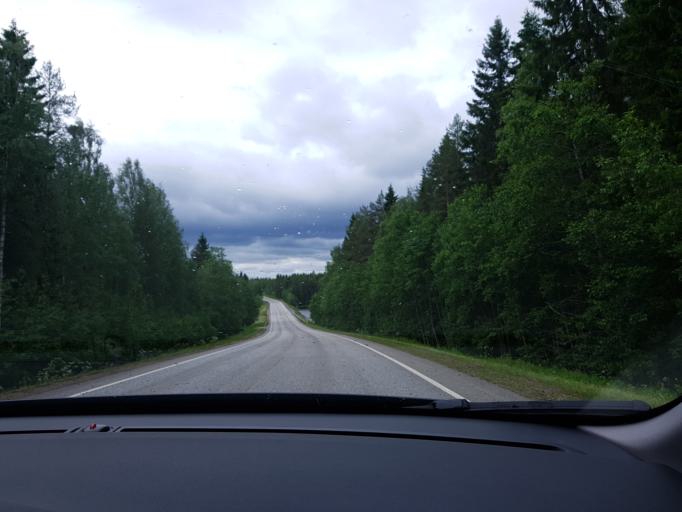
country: FI
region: Kainuu
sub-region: Kehys-Kainuu
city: Kuhmo
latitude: 64.1619
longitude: 29.4672
